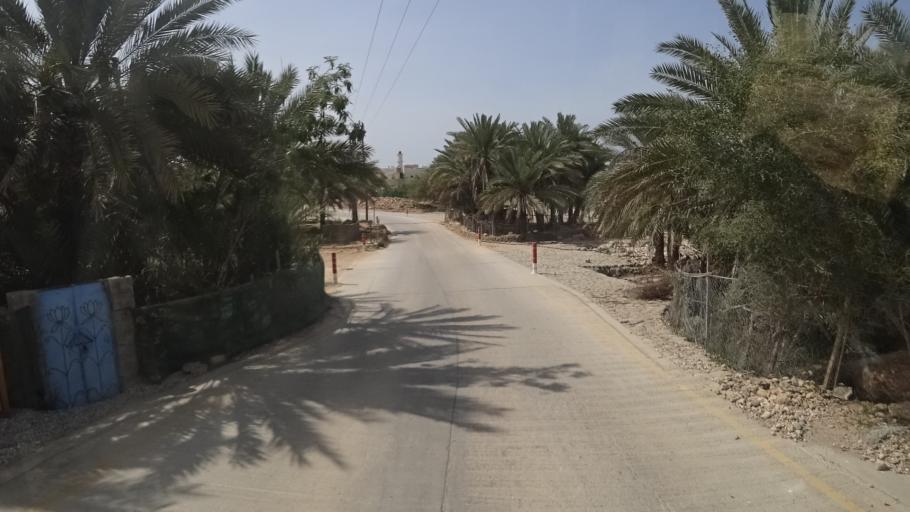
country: OM
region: Ash Sharqiyah
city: Sur
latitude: 22.9893
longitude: 59.1387
